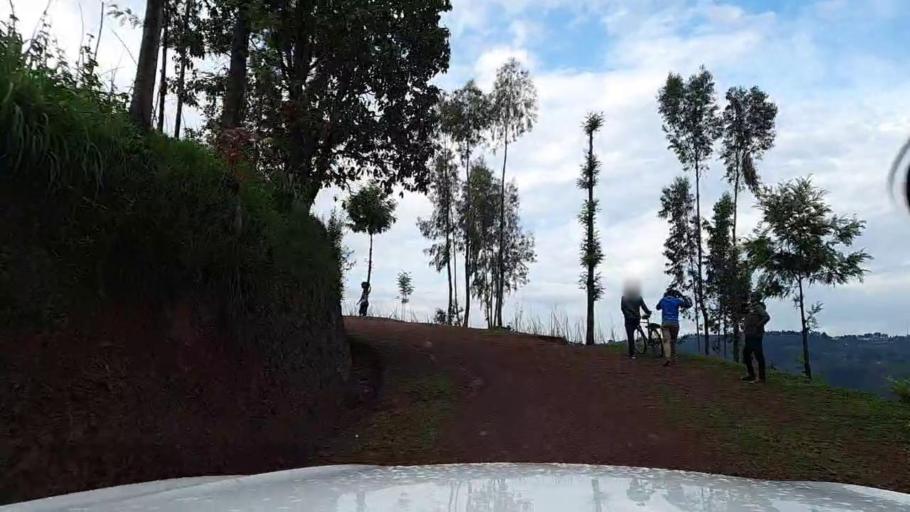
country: RW
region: Northern Province
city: Byumba
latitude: -1.7175
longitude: 29.9099
